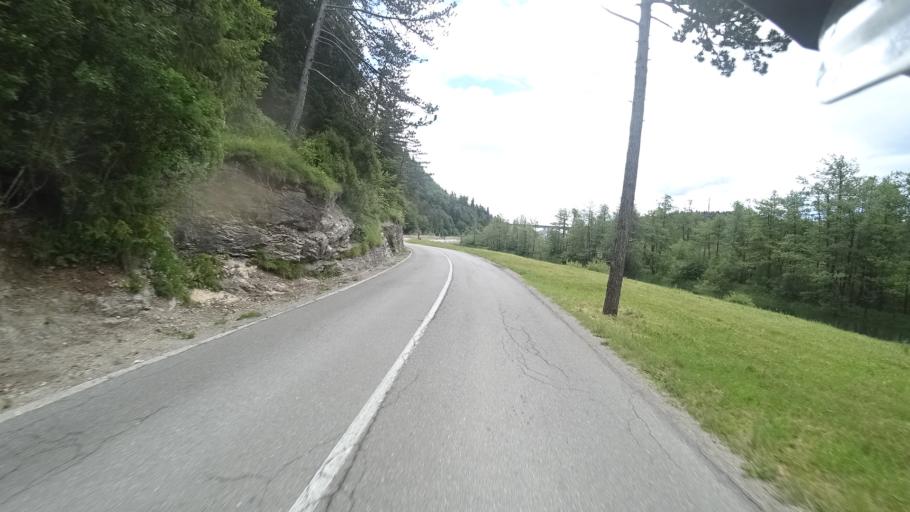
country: HR
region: Primorsko-Goranska
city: Hreljin
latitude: 45.3235
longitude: 14.7049
